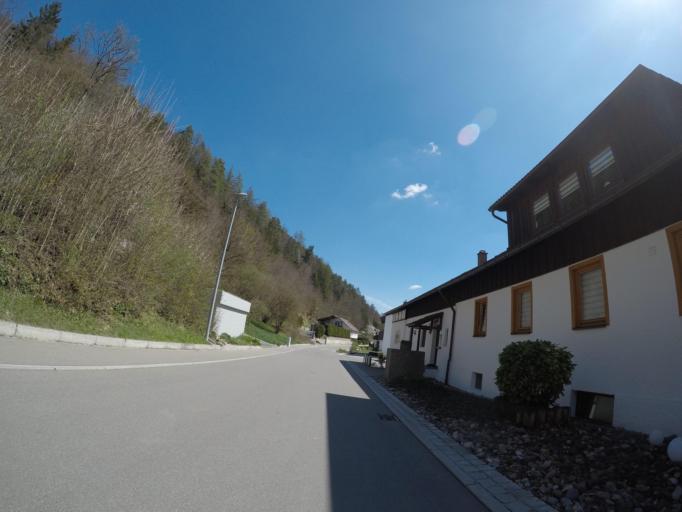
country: DE
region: Baden-Wuerttemberg
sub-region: Tuebingen Region
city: Blaubeuren
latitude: 48.4057
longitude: 9.7723
